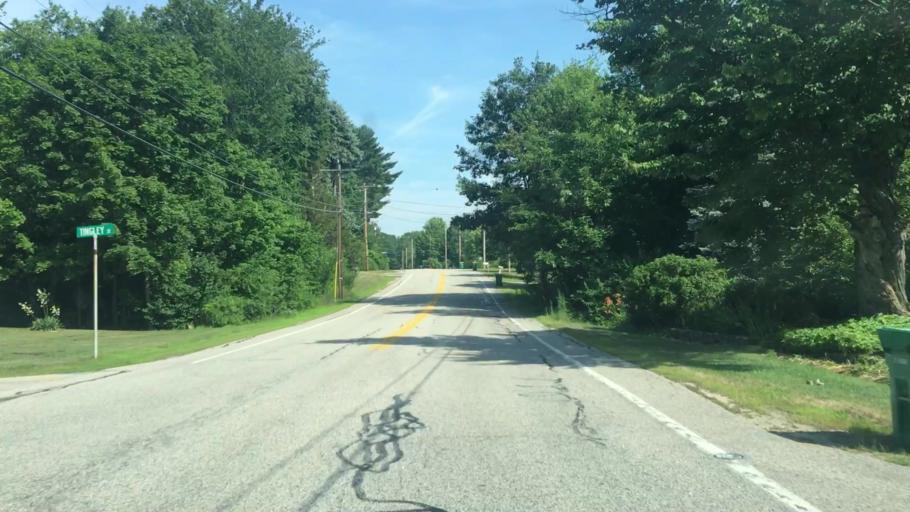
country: US
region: New Hampshire
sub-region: Strafford County
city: Rochester
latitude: 43.2774
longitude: -70.9640
